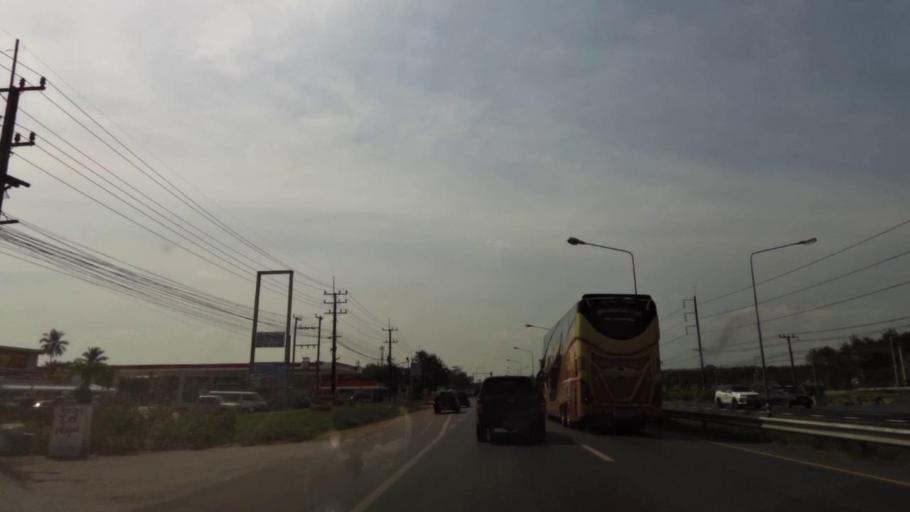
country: TH
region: Chanthaburi
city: Chanthaburi
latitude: 12.6621
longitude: 102.0745
